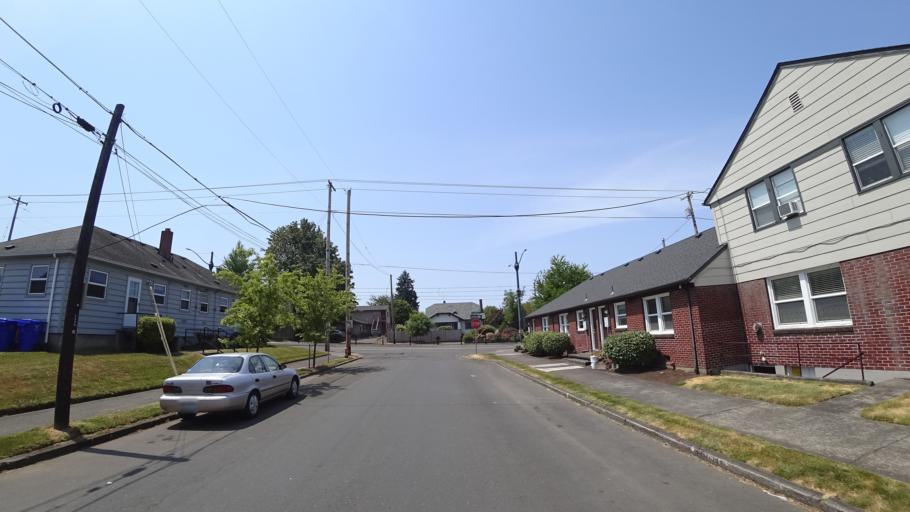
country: US
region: Oregon
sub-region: Multnomah County
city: Portland
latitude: 45.5794
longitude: -122.6814
